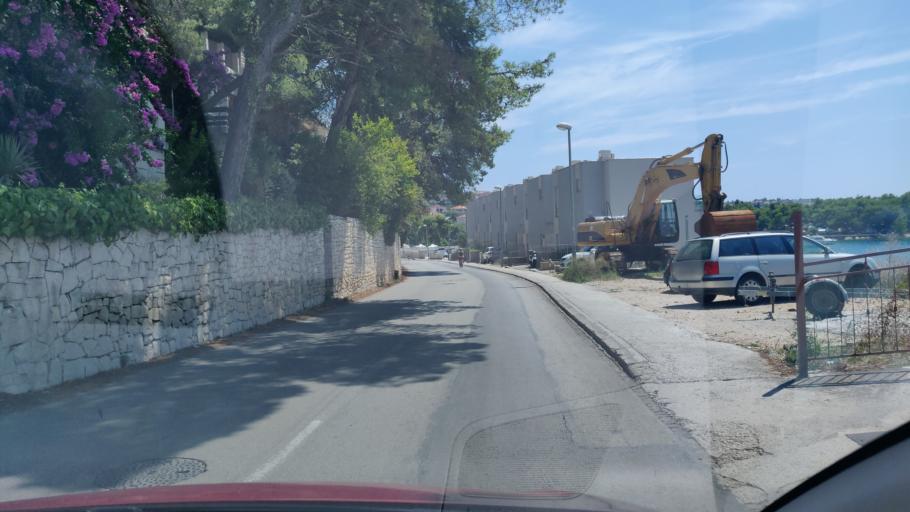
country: HR
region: Splitsko-Dalmatinska
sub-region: Grad Trogir
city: Trogir
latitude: 43.5090
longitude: 16.2561
